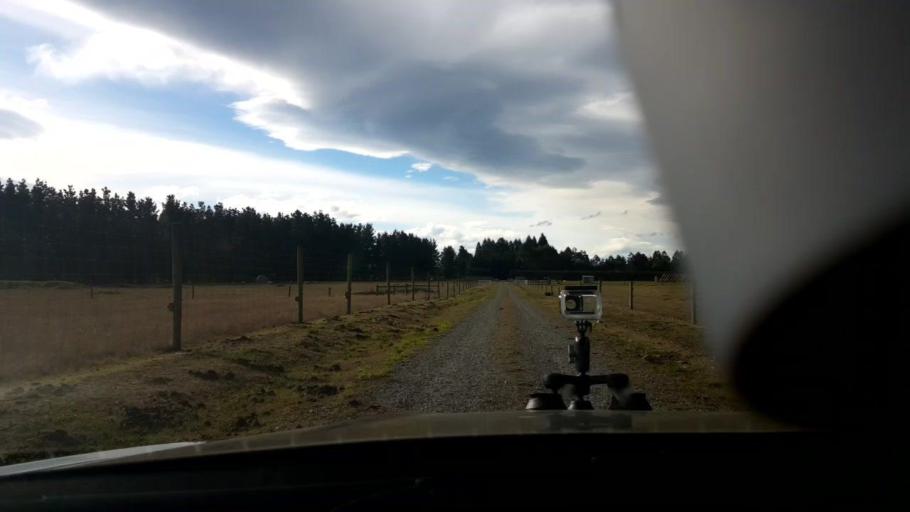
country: NZ
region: Canterbury
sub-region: Waimakariri District
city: Oxford
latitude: -43.4020
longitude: 172.3117
